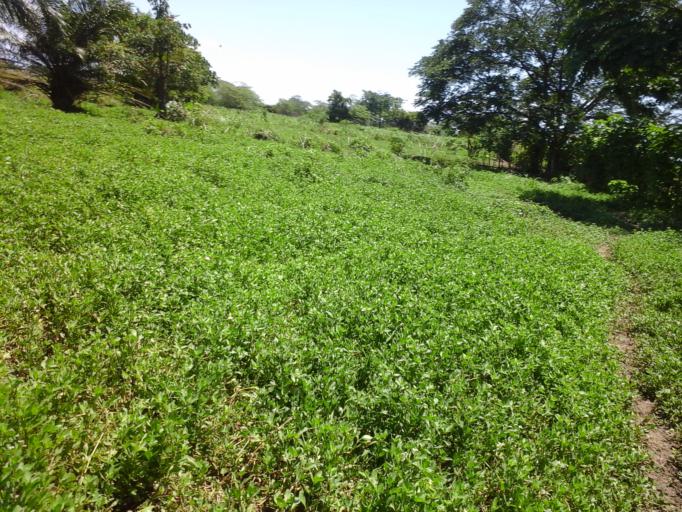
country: CO
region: Bolivar
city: Mahates
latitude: 10.1632
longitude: -75.2749
